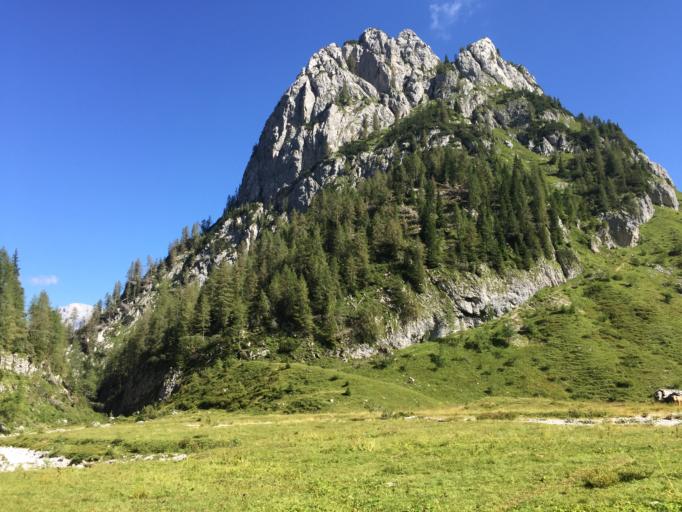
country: IT
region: Friuli Venezia Giulia
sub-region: Provincia di Udine
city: Forni Avoltri
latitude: 46.5491
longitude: 12.7417
